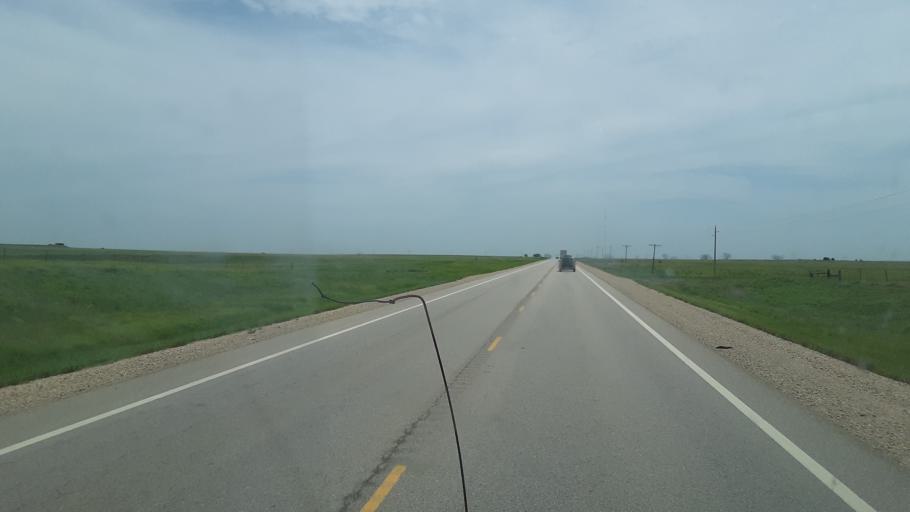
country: US
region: Kansas
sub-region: Greenwood County
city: Eureka
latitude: 37.8103
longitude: -96.4320
